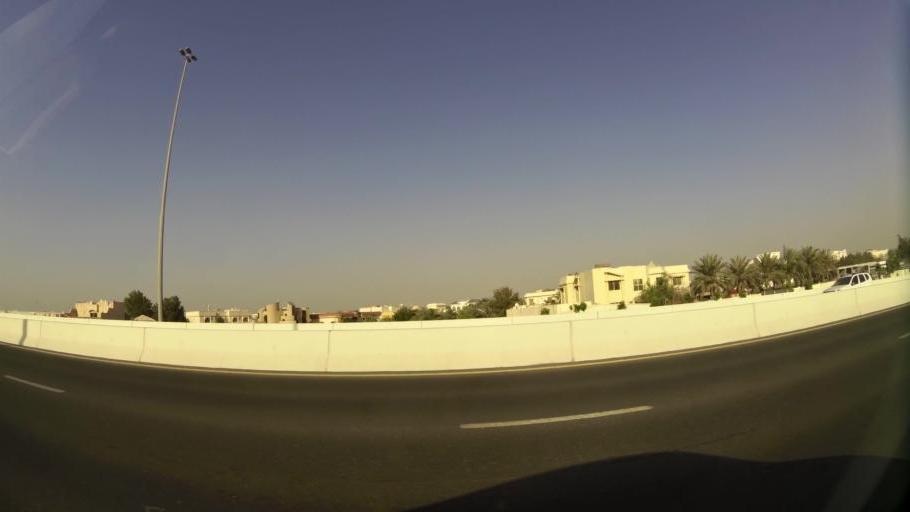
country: AE
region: Ash Shariqah
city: Sharjah
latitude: 25.2511
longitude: 55.3870
